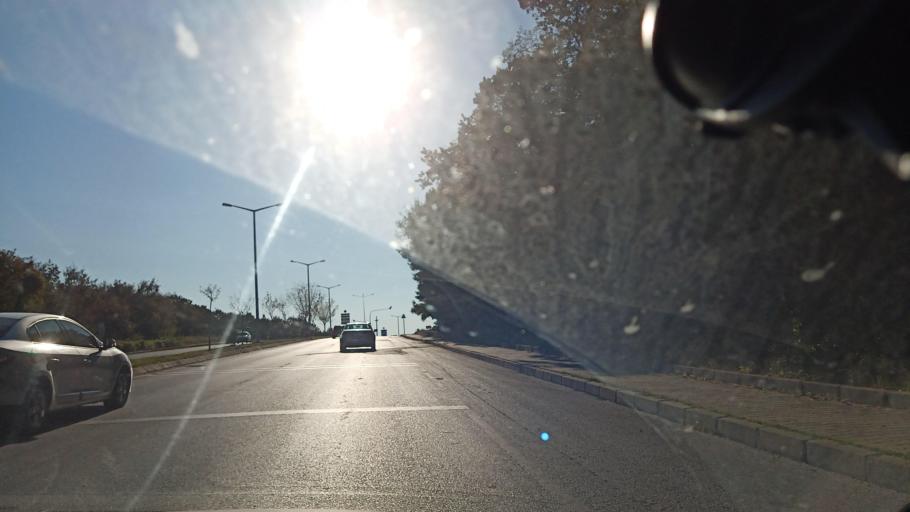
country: TR
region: Sakarya
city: Kazimpasa
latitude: 40.8542
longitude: 30.2953
